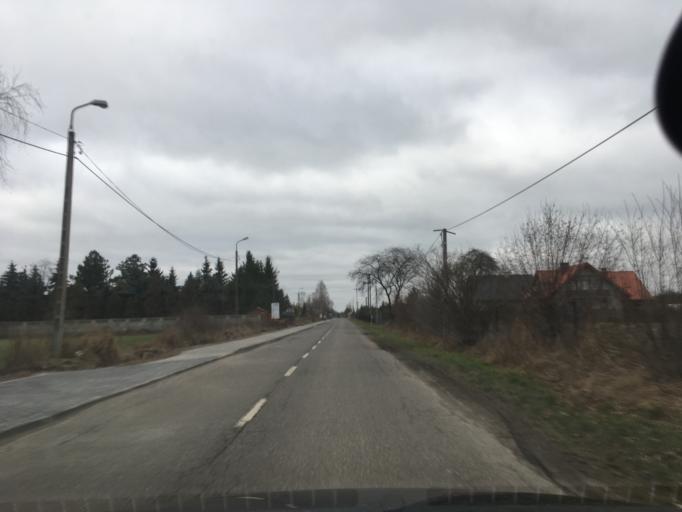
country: PL
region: Masovian Voivodeship
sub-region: Powiat piaseczynski
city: Lesznowola
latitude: 52.0424
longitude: 20.9542
